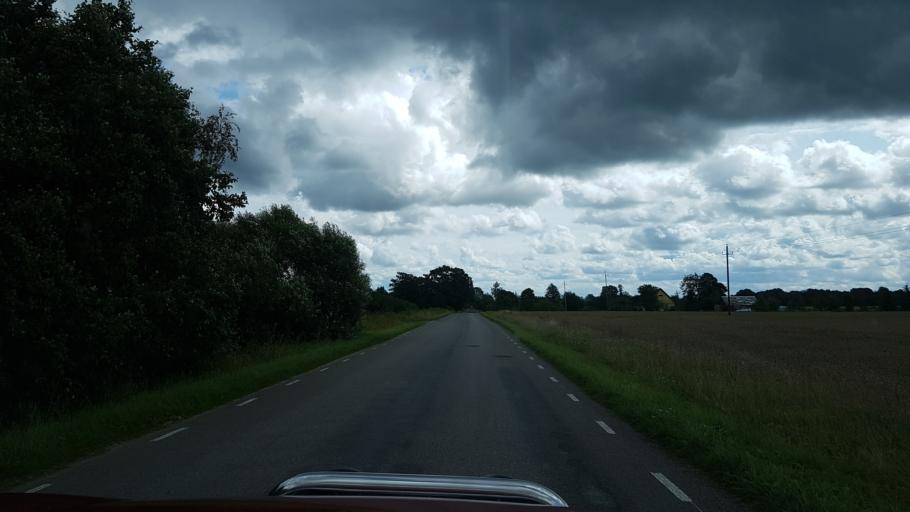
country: EE
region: Laeaene
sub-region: Lihula vald
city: Lihula
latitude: 58.7133
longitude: 24.0030
